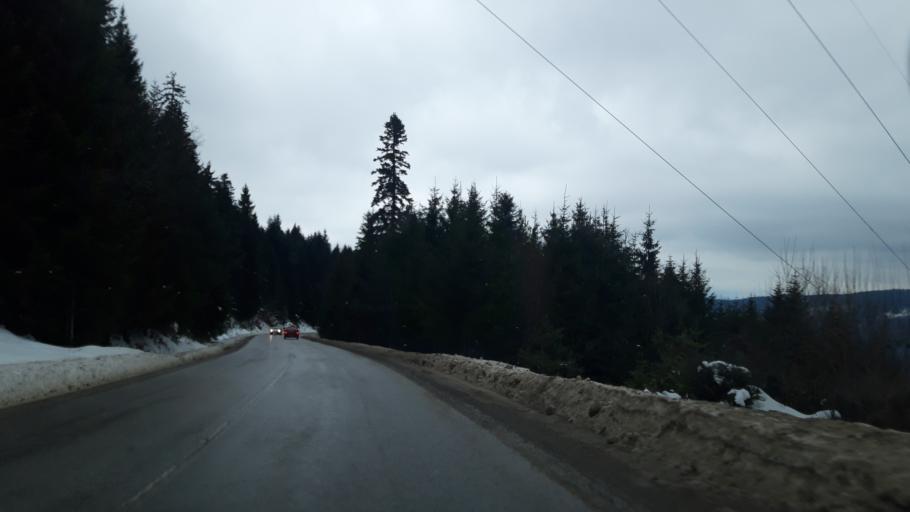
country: BA
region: Republika Srpska
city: Pale
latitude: 43.9145
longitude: 18.6462
